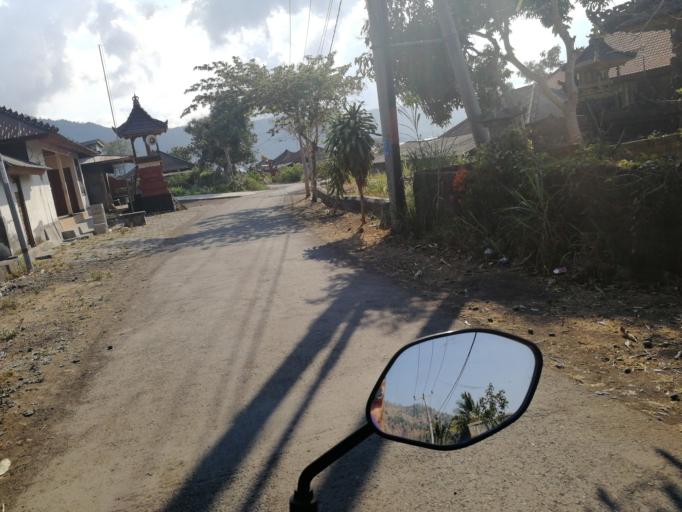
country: ID
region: Bali
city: Banjar Trunyan
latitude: -8.2715
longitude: 115.4152
